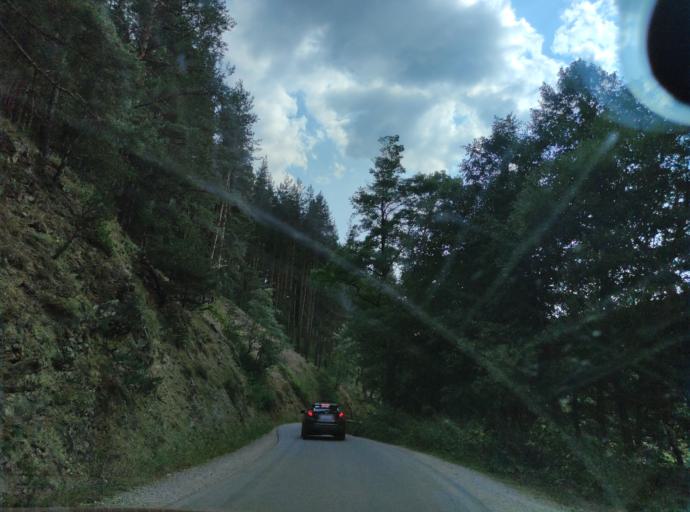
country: BG
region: Blagoevgrad
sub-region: Obshtina Belitsa
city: Belitsa
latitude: 41.9662
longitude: 23.5561
